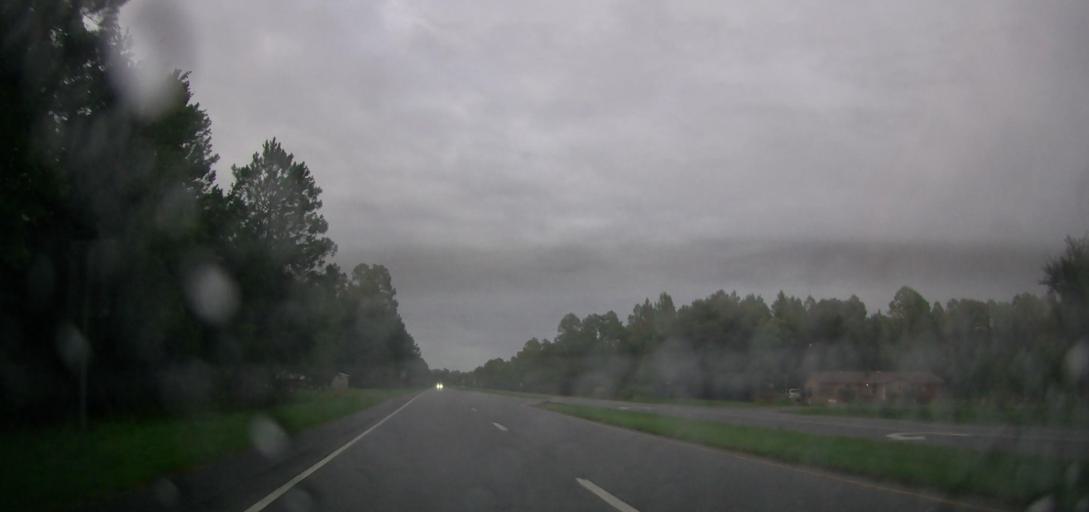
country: US
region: Georgia
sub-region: Clinch County
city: Homerville
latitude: 30.9931
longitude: -82.8670
